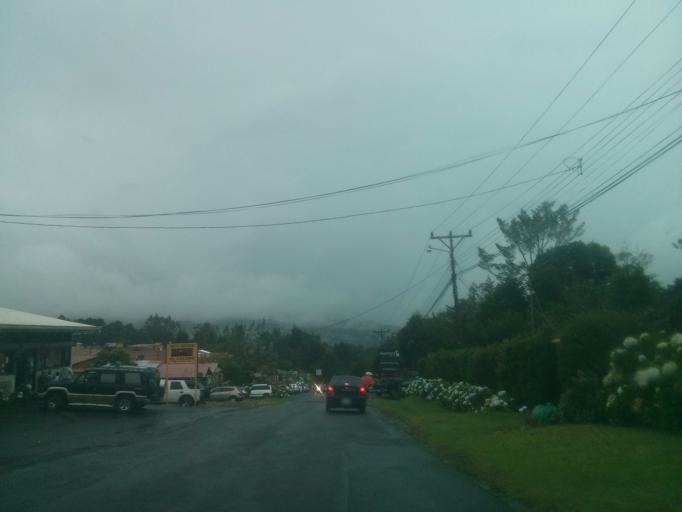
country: CR
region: Alajuela
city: Sabanilla
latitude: 10.1585
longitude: -84.1975
